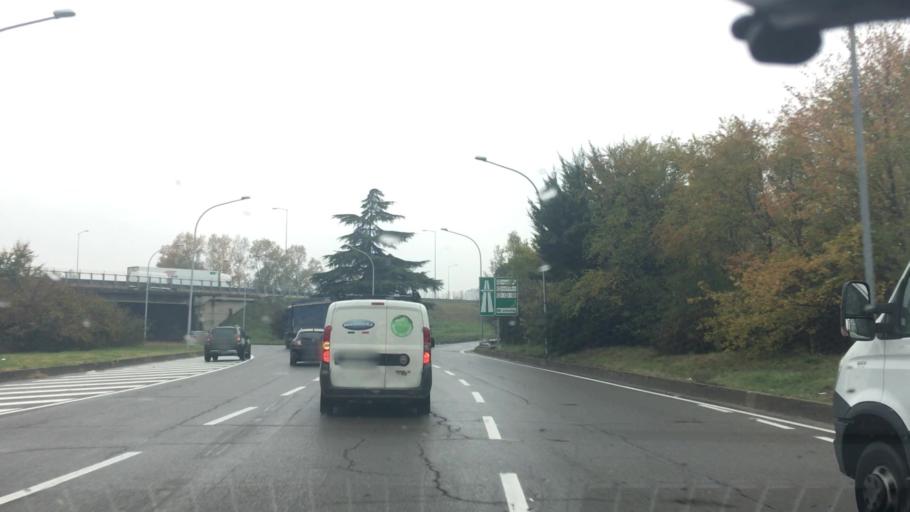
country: IT
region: Emilia-Romagna
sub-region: Provincia di Bologna
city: Casalecchio di Reno
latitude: 44.5101
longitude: 11.2774
